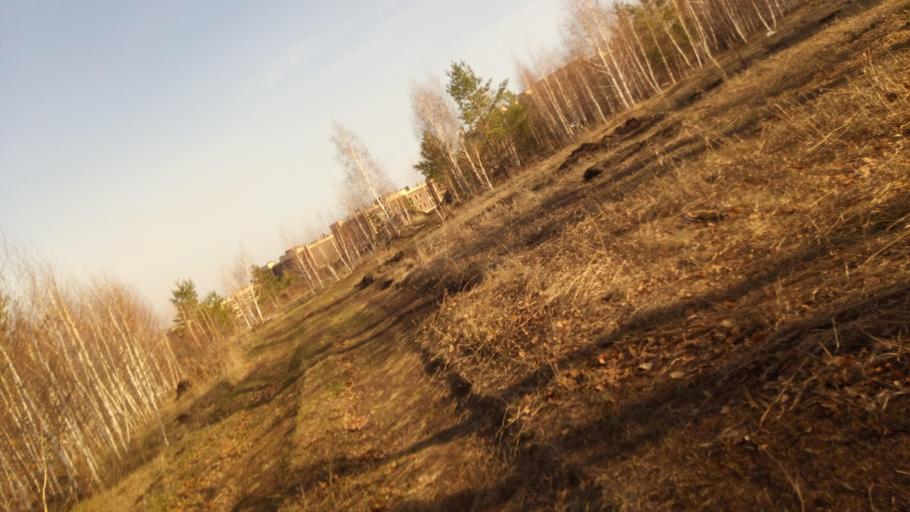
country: RU
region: Chelyabinsk
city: Sargazy
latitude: 55.1137
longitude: 61.2447
